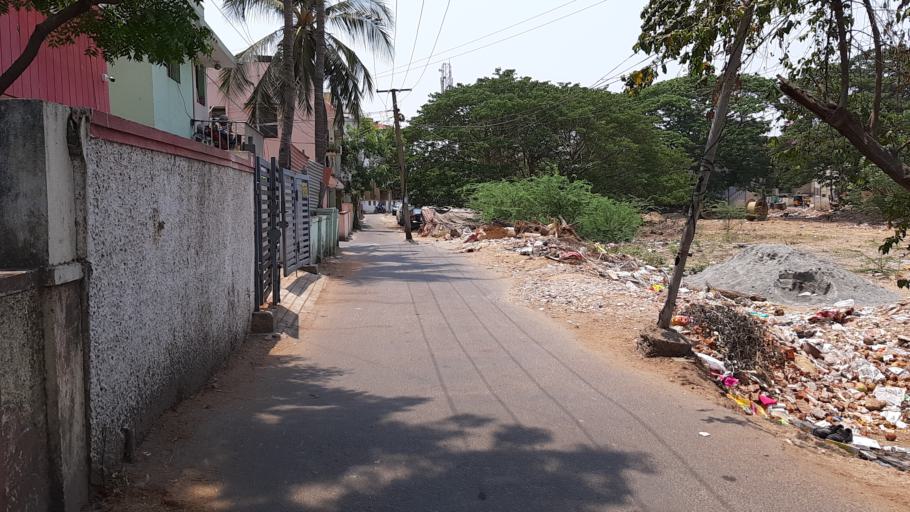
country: IN
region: Tamil Nadu
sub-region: Thiruvallur
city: Porur
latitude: 13.0547
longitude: 80.1965
